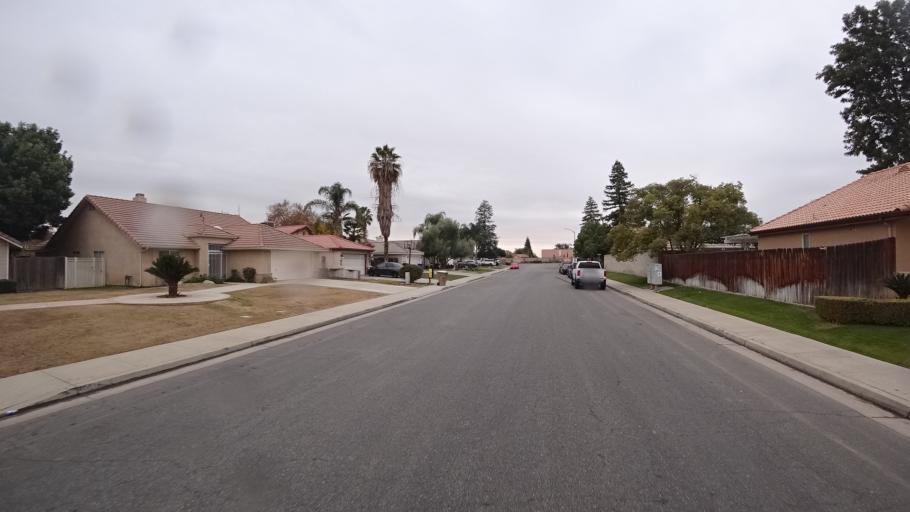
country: US
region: California
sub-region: Kern County
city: Greenfield
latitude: 35.2870
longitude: -119.0464
